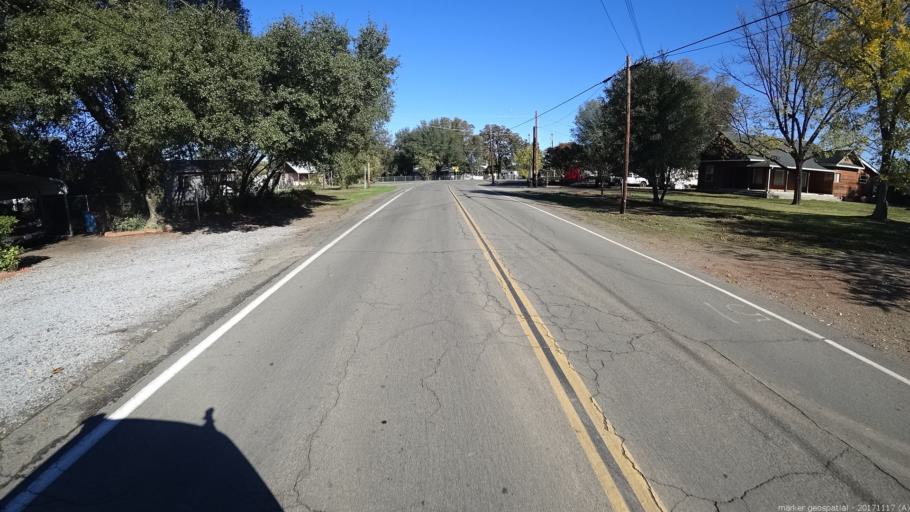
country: US
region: California
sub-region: Shasta County
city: Cottonwood
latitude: 40.3852
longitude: -122.2764
